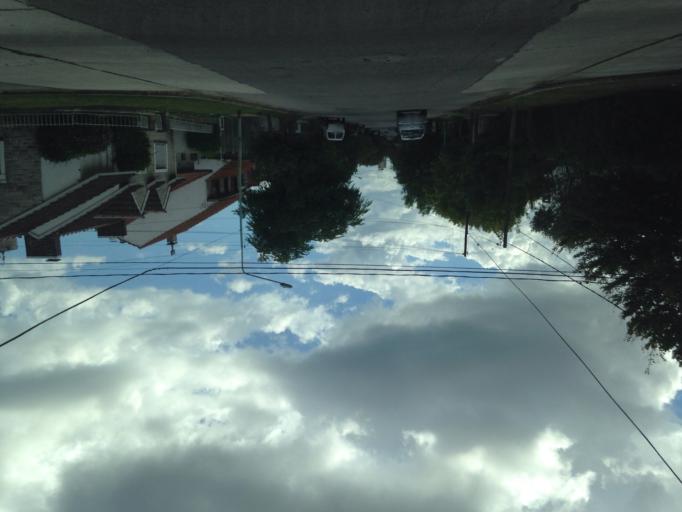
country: AR
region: Buenos Aires
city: Mar del Plata
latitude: -38.0188
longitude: -57.5512
